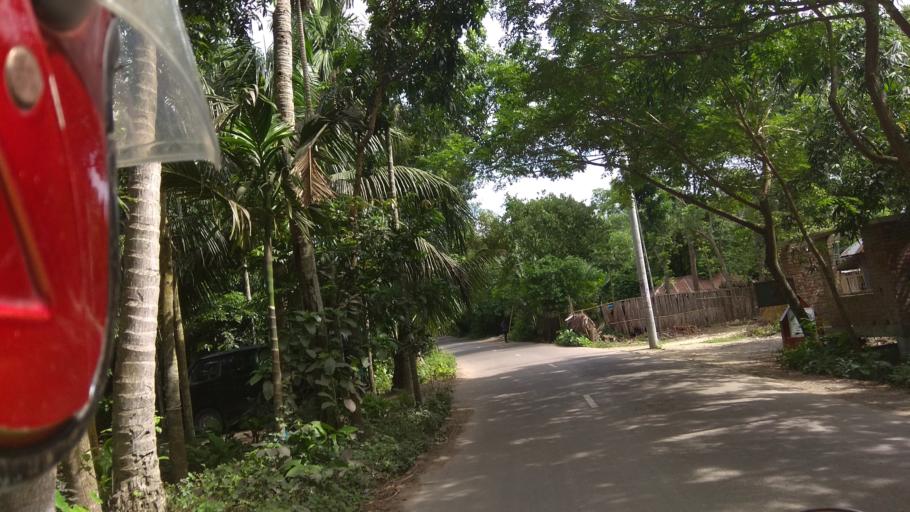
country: BD
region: Khulna
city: Kalia
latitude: 23.1545
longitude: 89.6446
